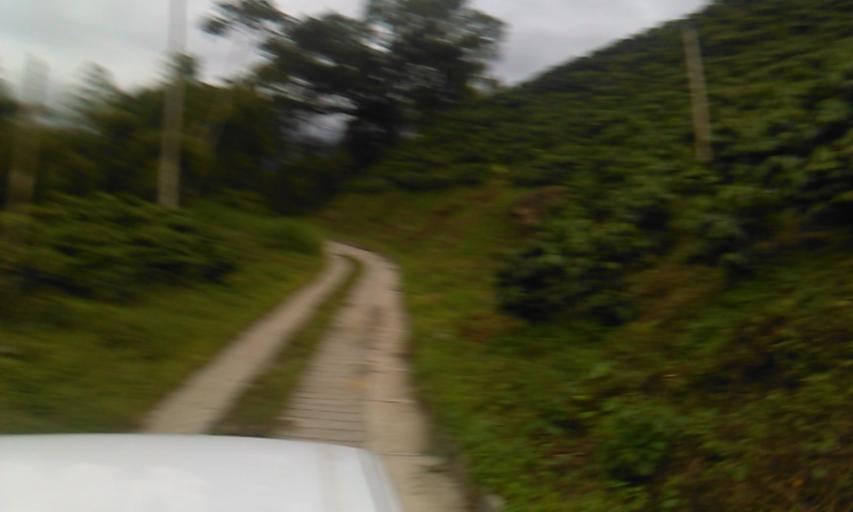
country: CO
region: Quindio
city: Cordoba
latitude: 4.4084
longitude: -75.6900
